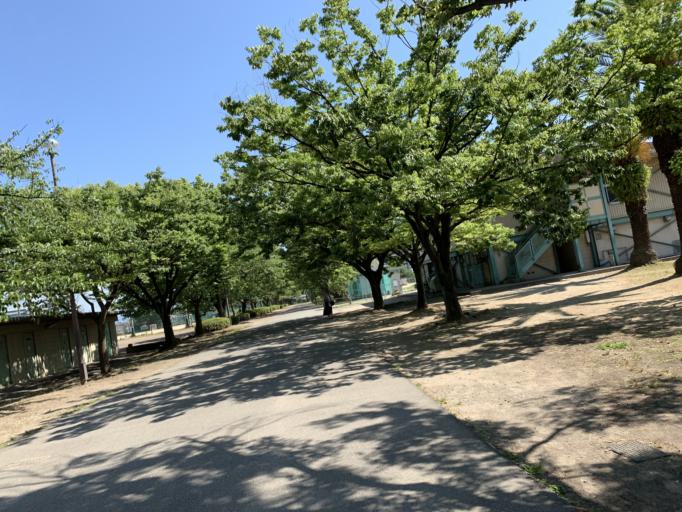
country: JP
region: Osaka
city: Sakai
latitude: 34.5898
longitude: 135.5044
